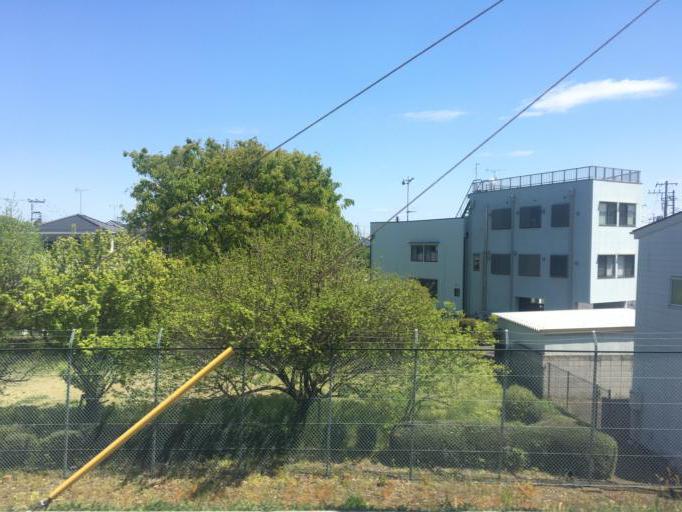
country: JP
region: Saitama
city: Kawagoe
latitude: 35.9296
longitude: 139.4359
